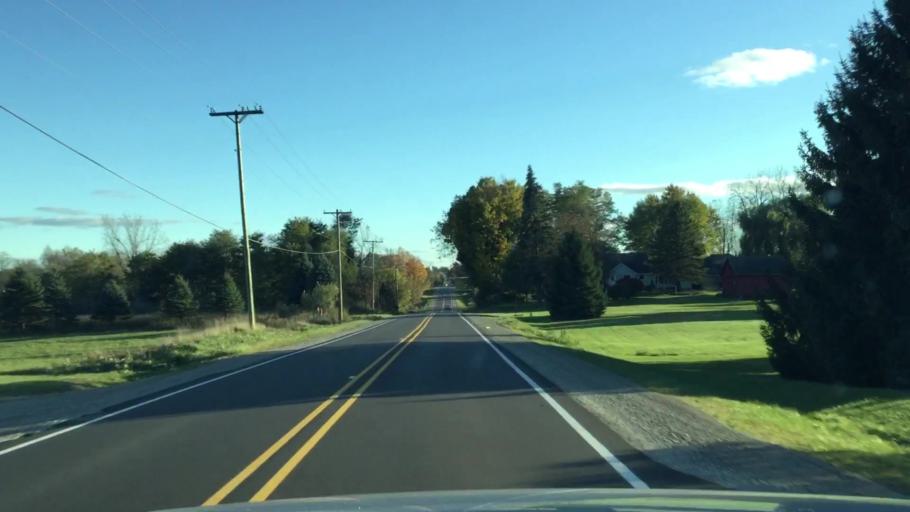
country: US
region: Michigan
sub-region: Lapeer County
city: Almont
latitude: 42.9364
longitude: -83.1444
